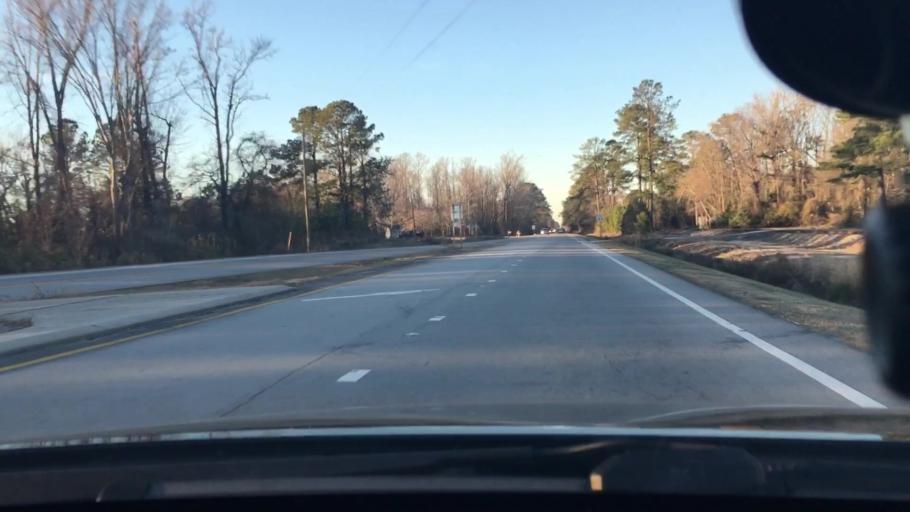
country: US
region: North Carolina
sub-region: Craven County
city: New Bern
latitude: 35.1585
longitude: -77.0366
